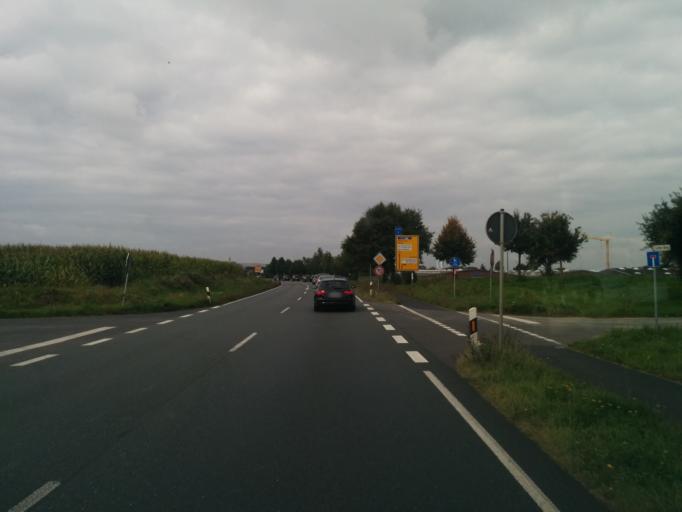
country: DE
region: North Rhine-Westphalia
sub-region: Regierungsbezirk Munster
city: Coesfeld
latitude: 51.9143
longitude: 7.1778
